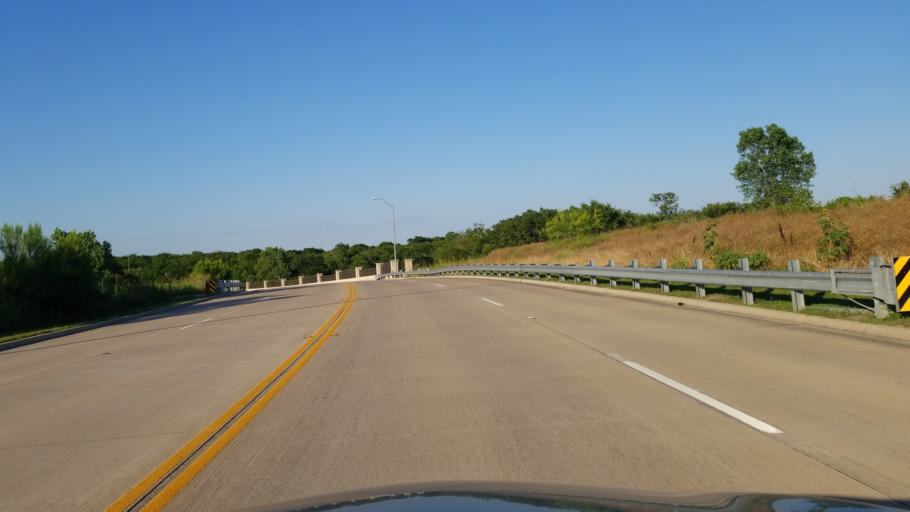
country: US
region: Texas
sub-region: Dallas County
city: Grand Prairie
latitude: 32.6775
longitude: -97.0318
